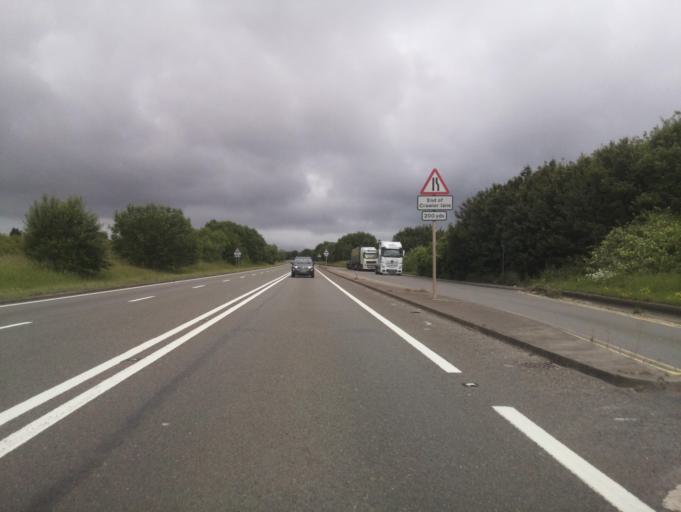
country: GB
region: England
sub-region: Leicestershire
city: Ashby de la Zouch
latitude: 52.7653
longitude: -1.4959
